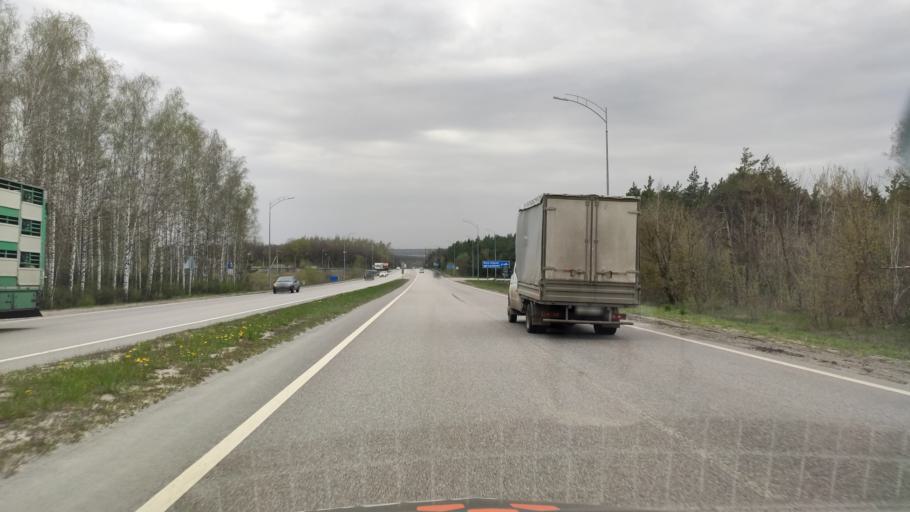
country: RU
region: Belgorod
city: Staryy Oskol
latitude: 51.3633
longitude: 37.8393
